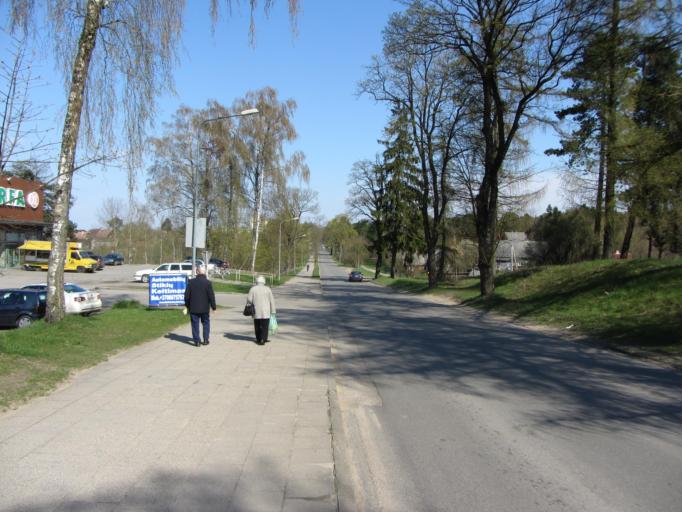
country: LT
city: Lentvaris
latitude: 54.6463
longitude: 25.0521
